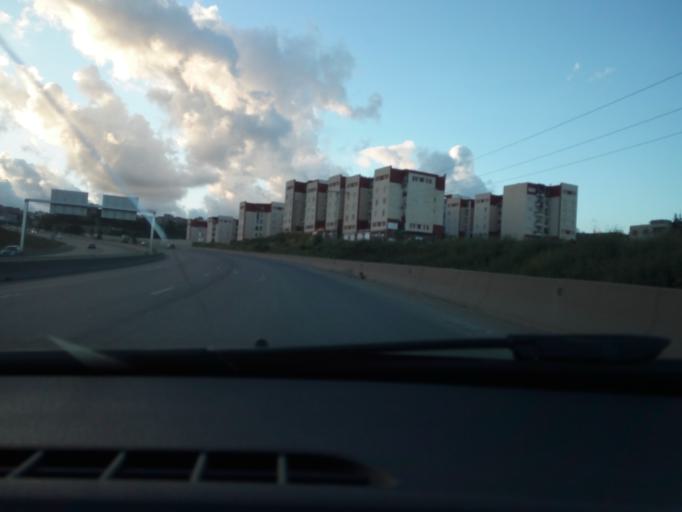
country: DZ
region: Tipaza
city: Saoula
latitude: 36.6567
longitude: 3.0107
